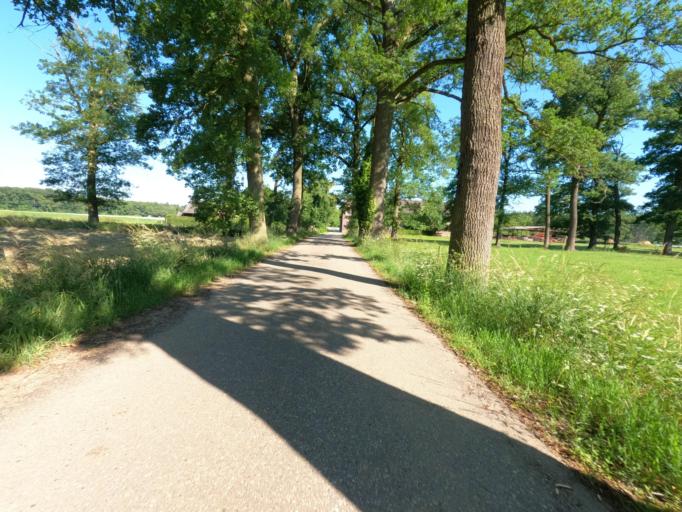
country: DE
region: North Rhine-Westphalia
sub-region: Regierungsbezirk Koln
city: Wassenberg
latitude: 51.1208
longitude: 6.1291
